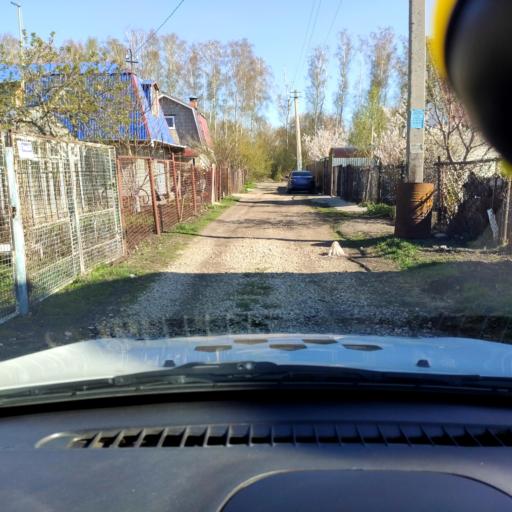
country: RU
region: Samara
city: Tol'yatti
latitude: 53.5995
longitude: 49.2945
